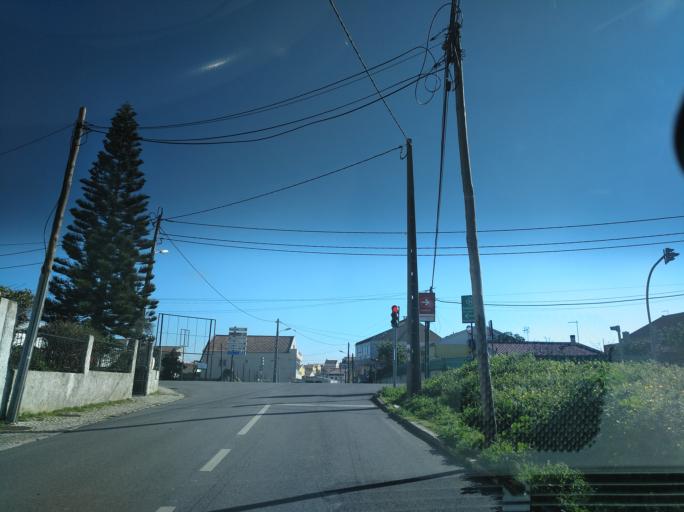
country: PT
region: Lisbon
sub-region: Odivelas
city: Canecas
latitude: 38.8082
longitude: -9.2206
